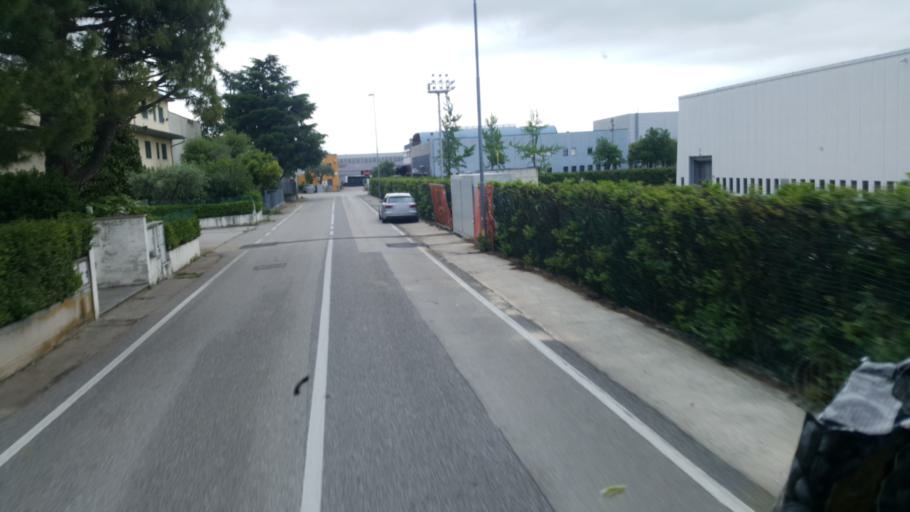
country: IT
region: Veneto
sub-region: Provincia di Vicenza
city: Santorso
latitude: 45.7208
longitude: 11.3917
